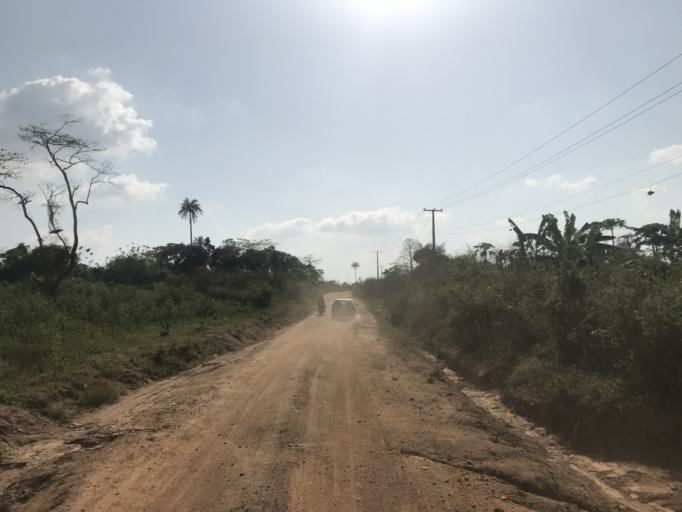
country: NG
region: Osun
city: Osogbo
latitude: 7.8511
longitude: 4.5853
